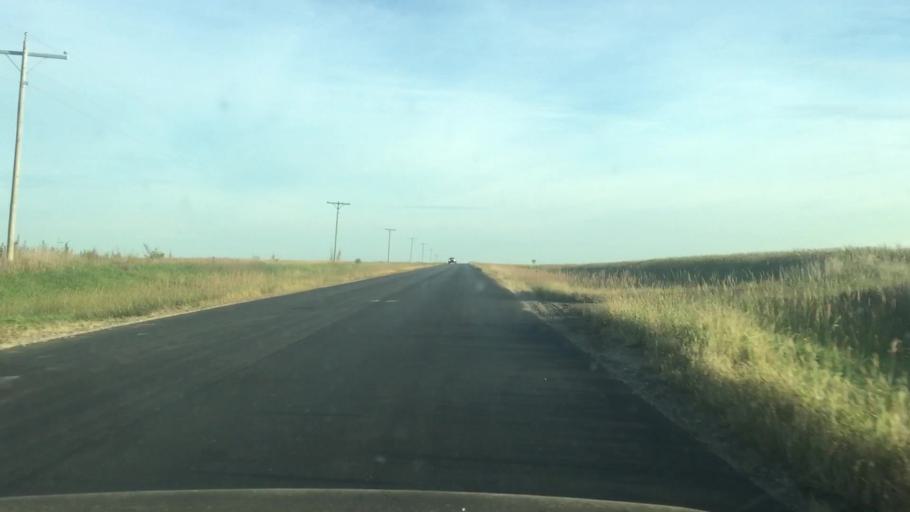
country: US
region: Kansas
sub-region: Marshall County
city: Marysville
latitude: 39.8635
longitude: -96.6009
